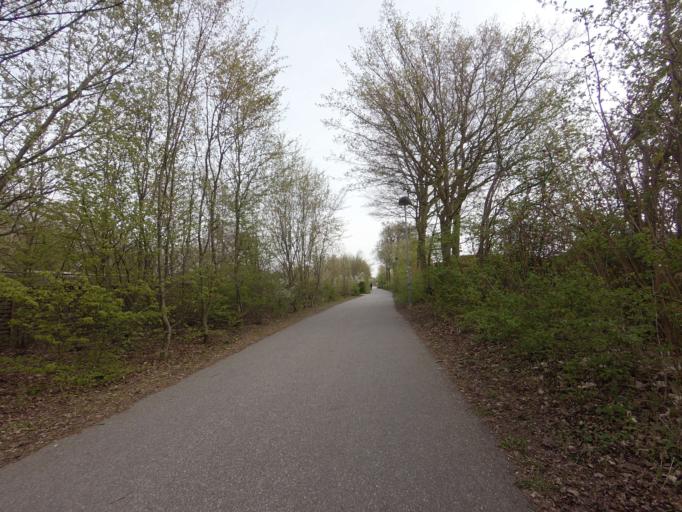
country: SE
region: Skane
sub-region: Lunds Kommun
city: Lund
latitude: 55.7208
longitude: 13.1741
